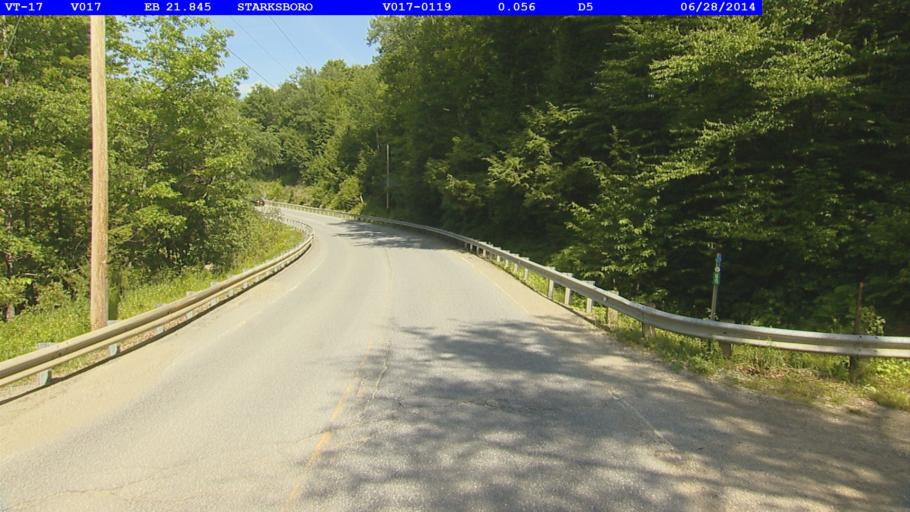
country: US
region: Vermont
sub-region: Addison County
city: Bristol
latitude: 44.1618
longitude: -73.0162
